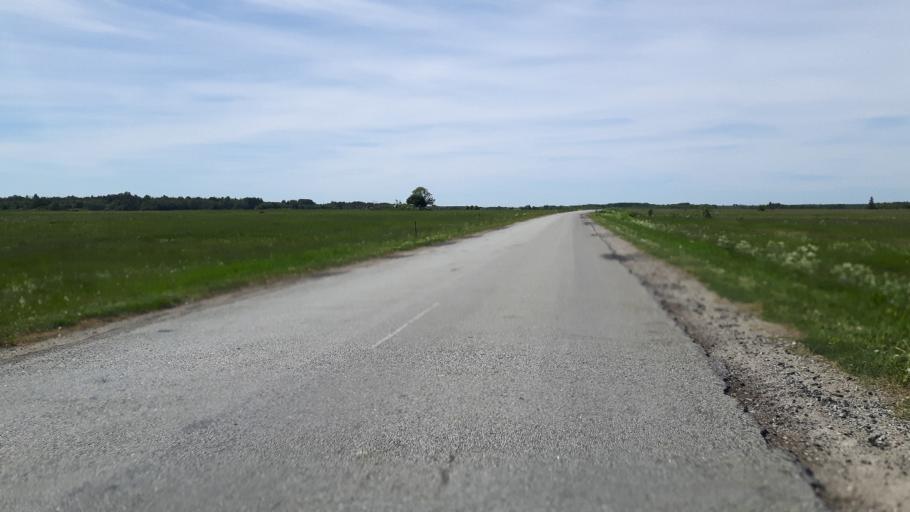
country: EE
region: Harju
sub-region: Kuusalu vald
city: Kuusalu
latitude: 59.4595
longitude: 25.3431
